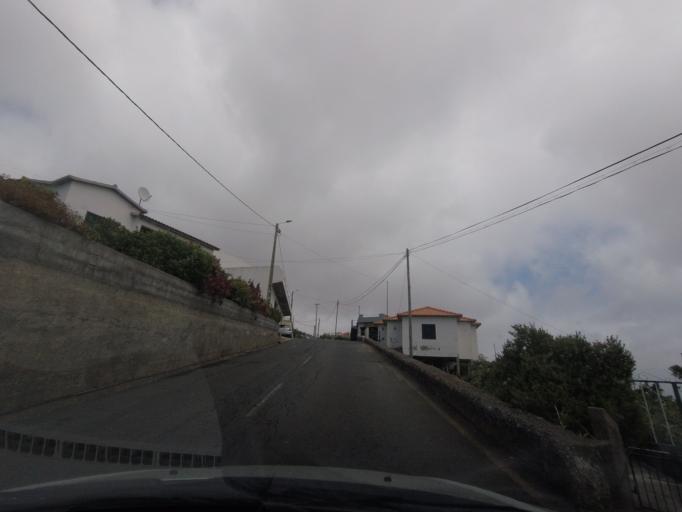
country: PT
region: Madeira
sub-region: Machico
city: Machico
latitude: 32.7016
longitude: -16.7770
